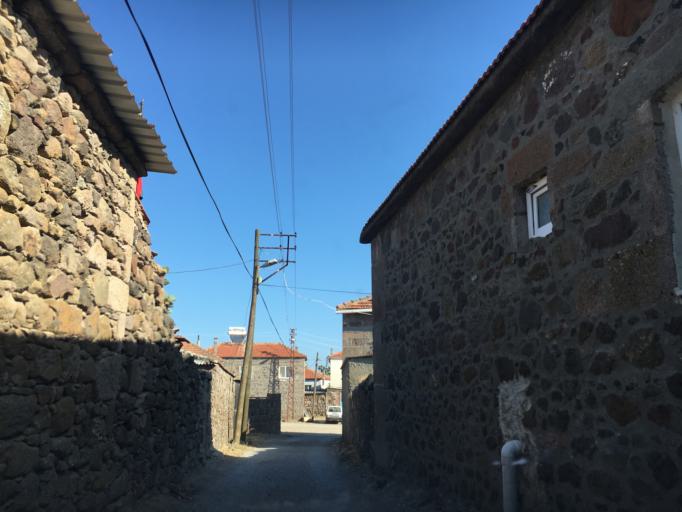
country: TR
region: Canakkale
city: Behram
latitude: 39.5039
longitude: 26.2552
